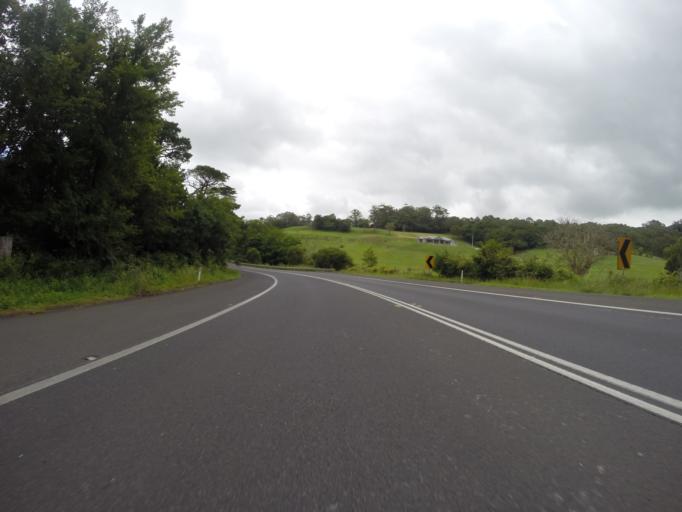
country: AU
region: New South Wales
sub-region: Shoalhaven Shire
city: Berry
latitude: -34.7475
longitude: 150.7514
